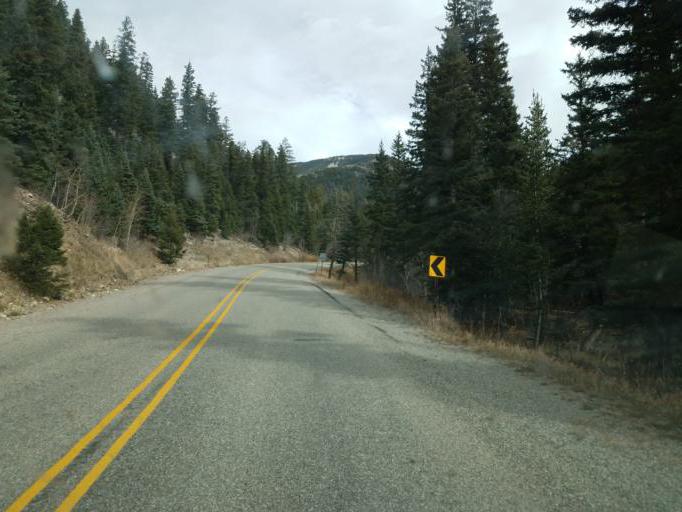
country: US
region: New Mexico
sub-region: Taos County
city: Arroyo Seco
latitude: 36.5893
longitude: -105.4898
